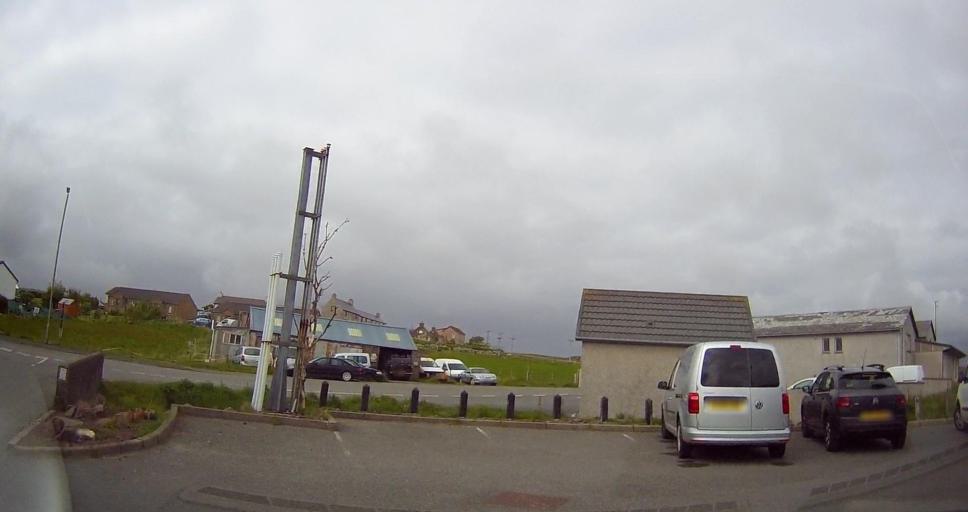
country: GB
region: Scotland
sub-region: Shetland Islands
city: Sandwick
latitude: 60.2288
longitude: -1.5632
